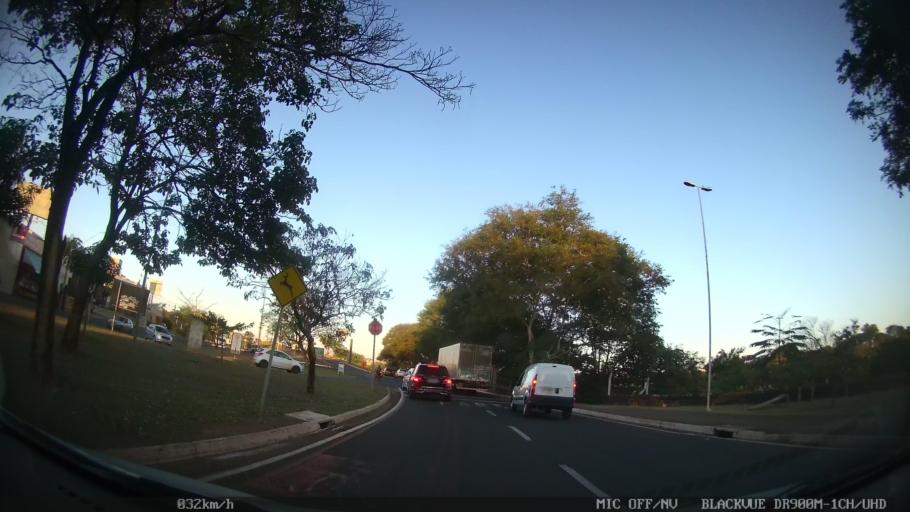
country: BR
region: Sao Paulo
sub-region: Sao Jose Do Rio Preto
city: Sao Jose do Rio Preto
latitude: -20.8088
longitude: -49.3579
